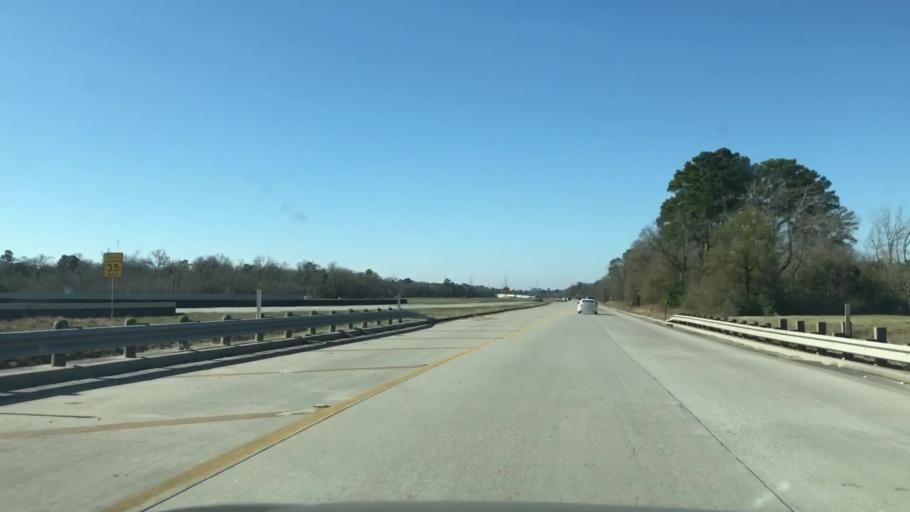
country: US
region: Texas
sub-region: Harris County
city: Cloverleaf
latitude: 29.8279
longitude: -95.1879
